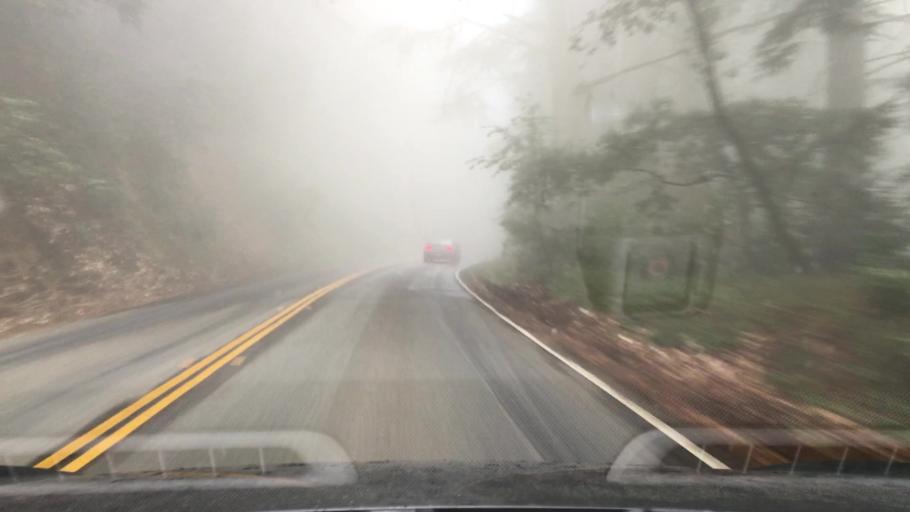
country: US
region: California
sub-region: San Mateo County
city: Woodside
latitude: 37.4220
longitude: -122.3193
